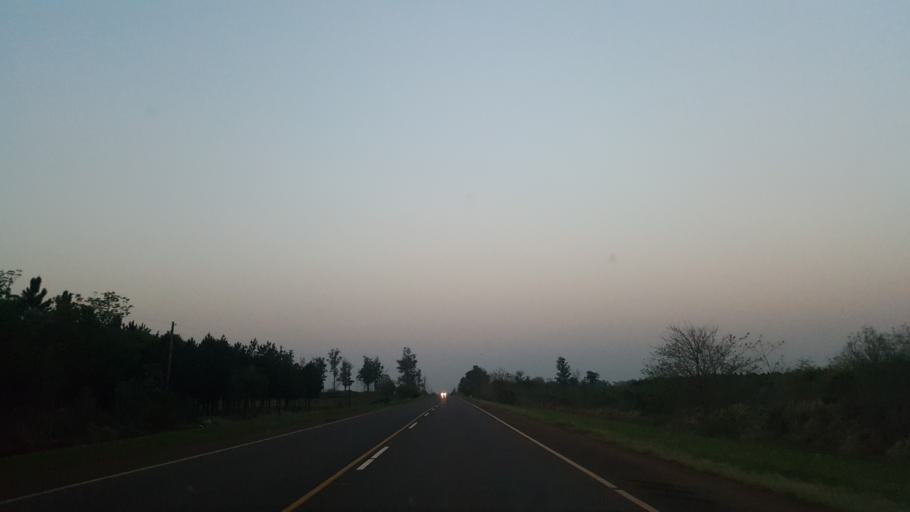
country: AR
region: Misiones
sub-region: Departamento de Capital
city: Posadas
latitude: -27.4252
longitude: -55.9992
